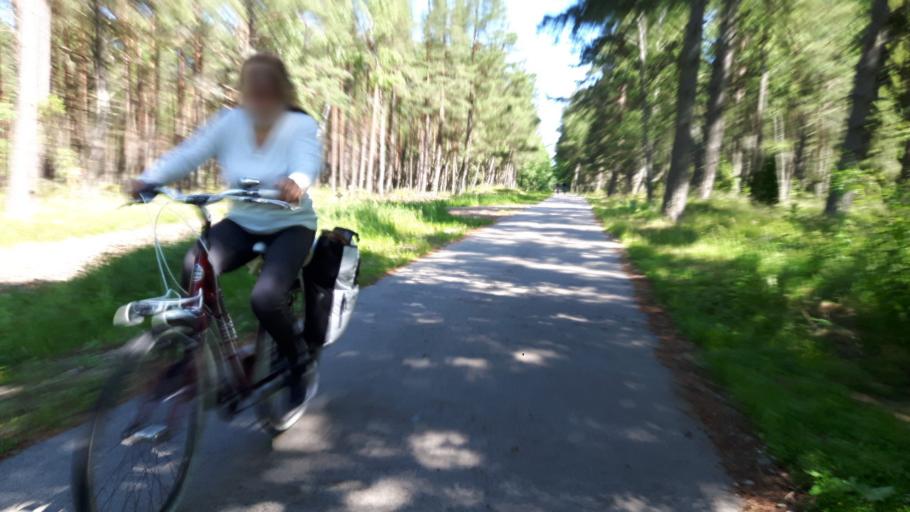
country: LT
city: Neringa
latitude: 55.3509
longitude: 21.0461
